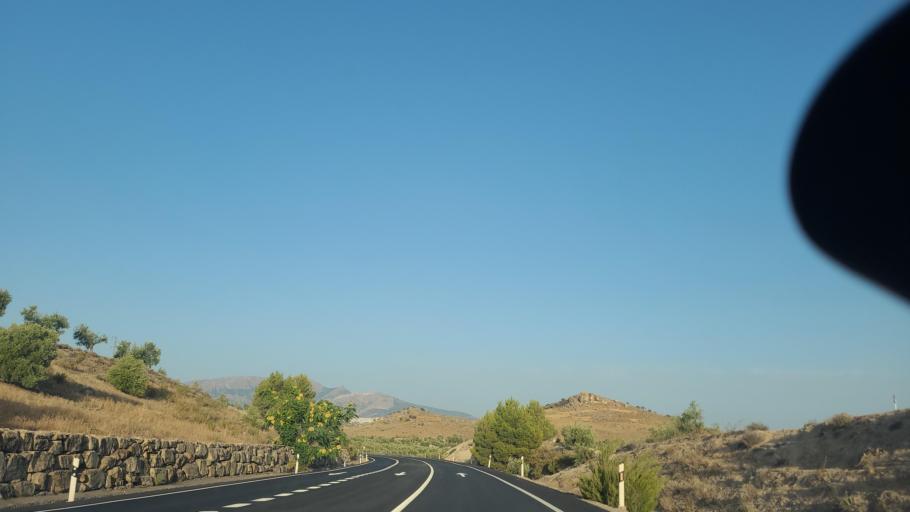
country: ES
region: Andalusia
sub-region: Provincia de Jaen
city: Mancha Real
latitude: 37.8048
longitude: -3.6539
